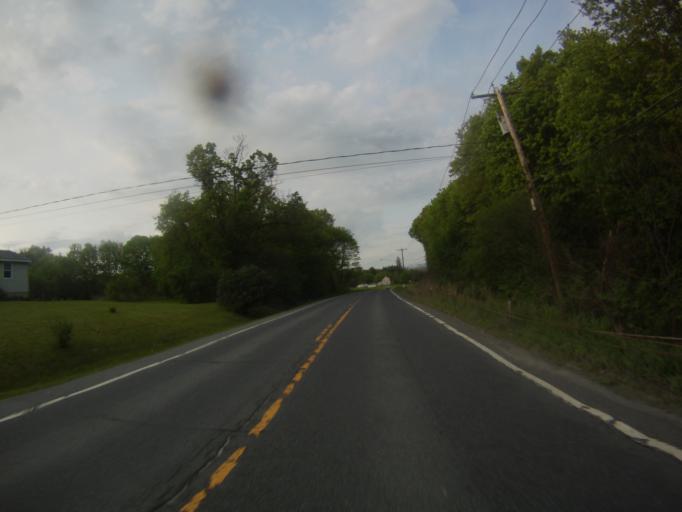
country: US
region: New York
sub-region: Essex County
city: Ticonderoga
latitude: 43.8902
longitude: -73.4440
